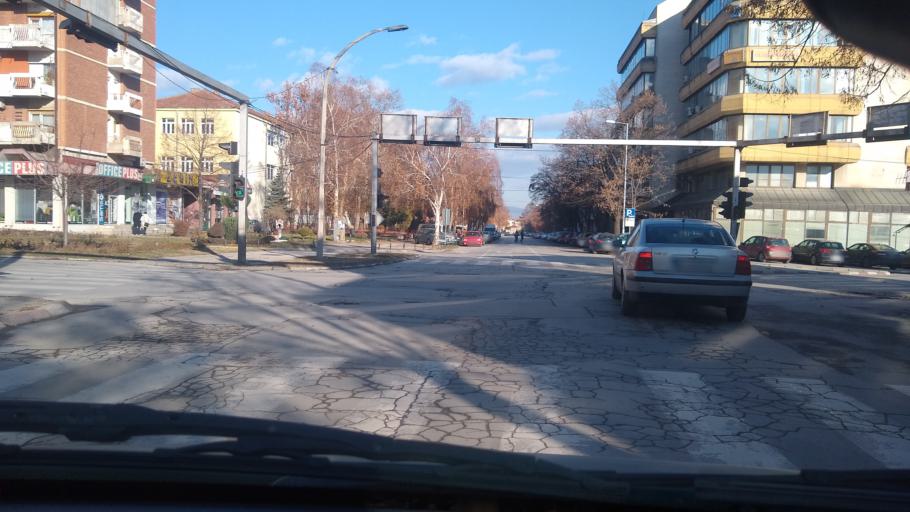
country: MK
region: Bitola
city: Bitola
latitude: 41.0283
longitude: 21.3376
